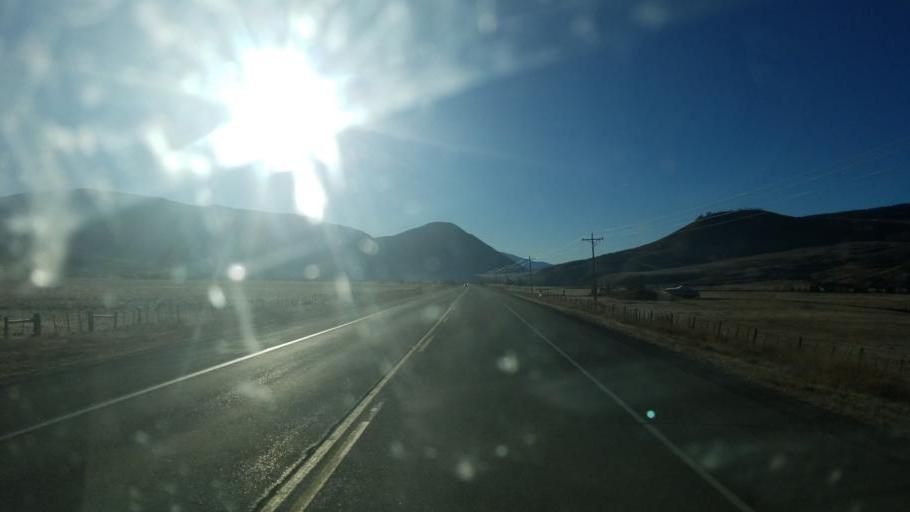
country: US
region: Colorado
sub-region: Gunnison County
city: Crested Butte
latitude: 38.8335
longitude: -106.9295
